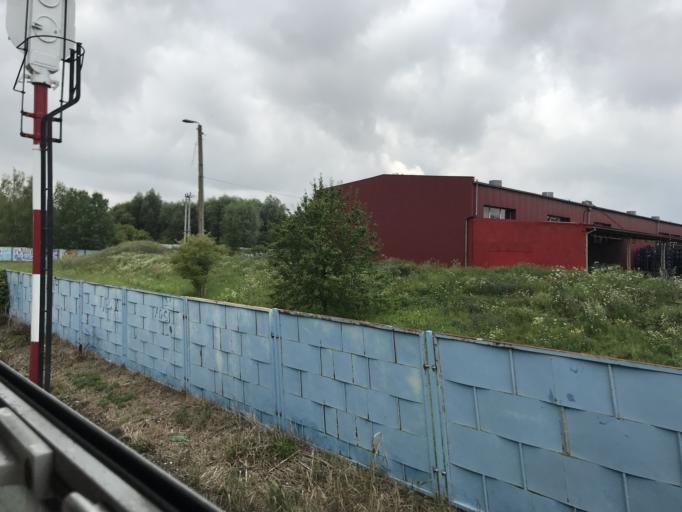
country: PL
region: Pomeranian Voivodeship
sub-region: Powiat malborski
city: Stare Pole
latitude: 54.0517
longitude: 19.1972
